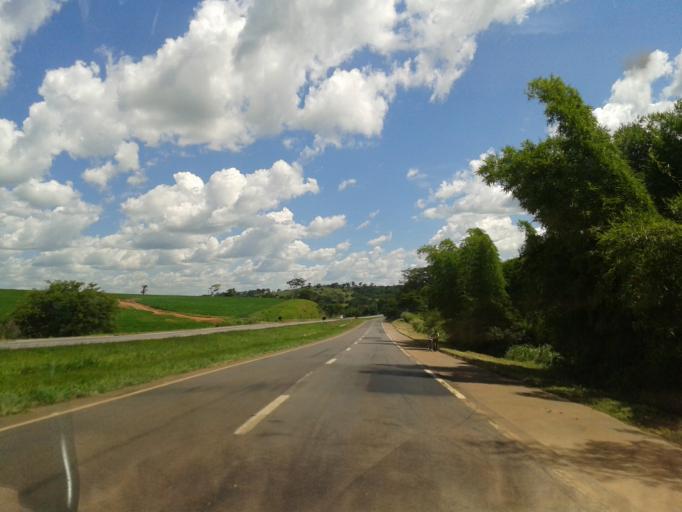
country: BR
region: Goias
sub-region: Piracanjuba
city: Piracanjuba
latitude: -17.1953
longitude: -49.2088
